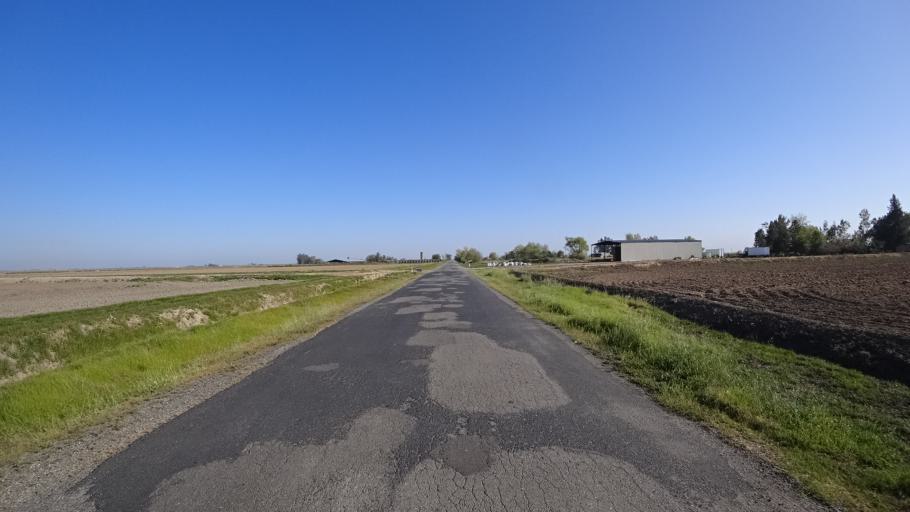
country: US
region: California
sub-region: Glenn County
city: Willows
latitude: 39.5470
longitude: -122.1029
